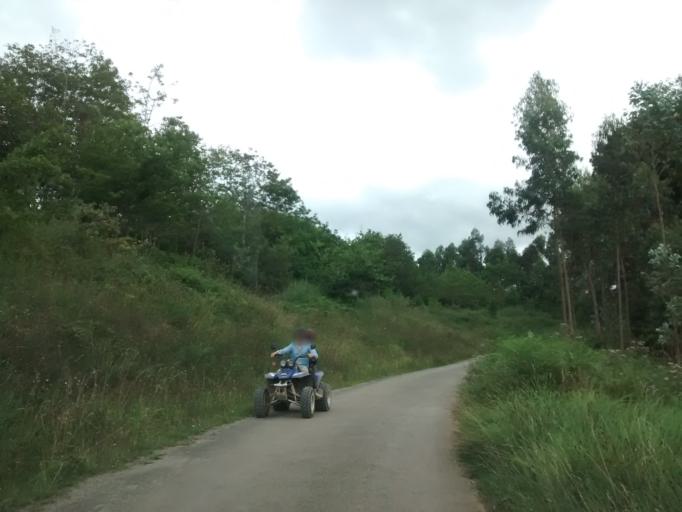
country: ES
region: Cantabria
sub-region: Provincia de Cantabria
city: Comillas
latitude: 43.3413
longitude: -4.2924
